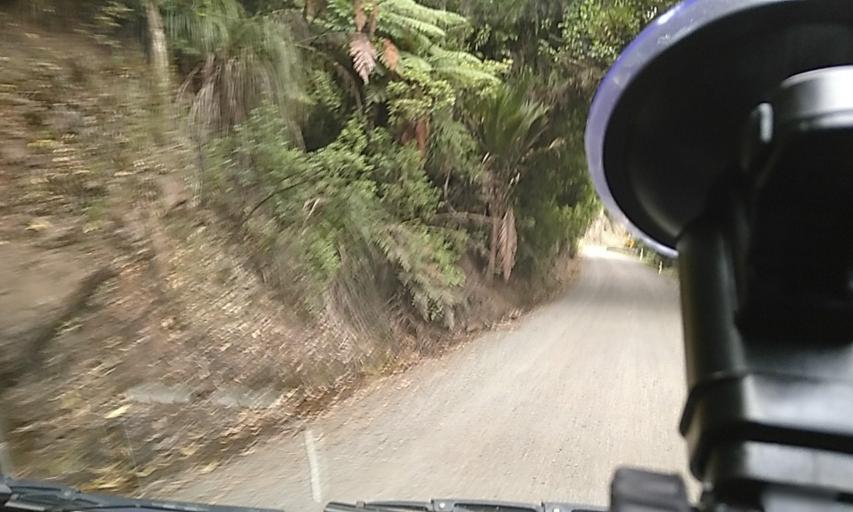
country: NZ
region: Northland
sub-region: Kaipara District
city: Dargaville
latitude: -35.6531
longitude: 173.5636
